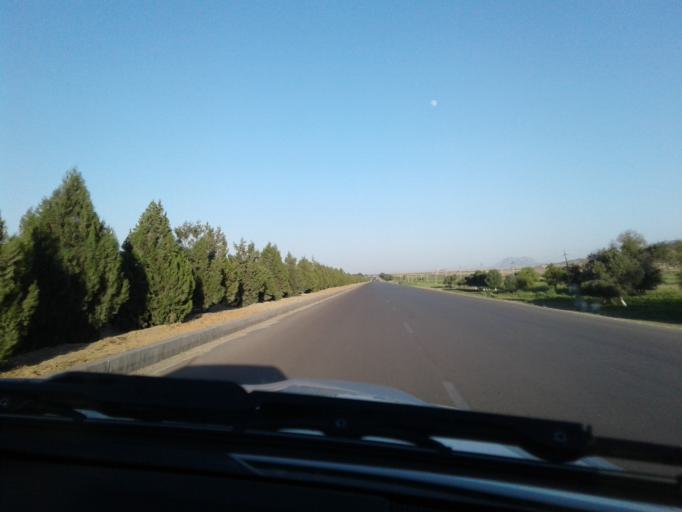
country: TM
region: Ahal
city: Baharly
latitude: 38.2600
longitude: 57.7275
